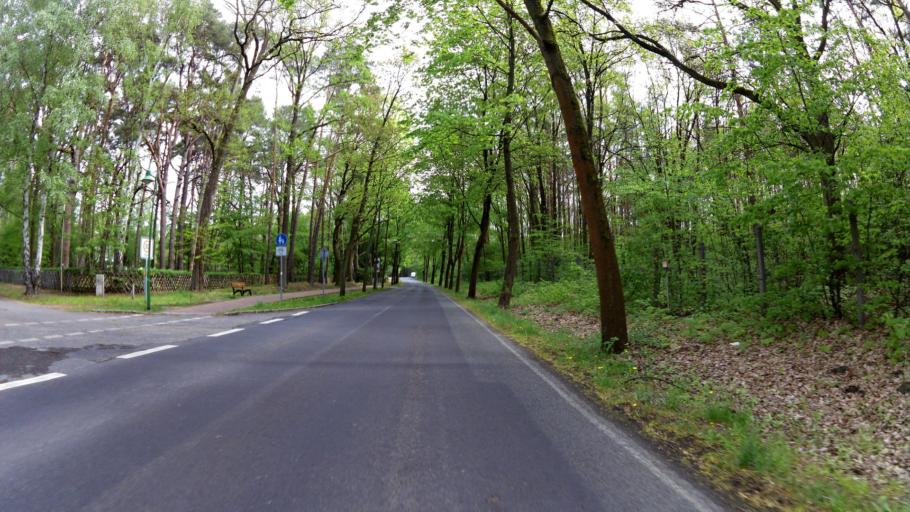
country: DE
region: Brandenburg
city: Bestensee
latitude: 52.2873
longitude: 13.6794
